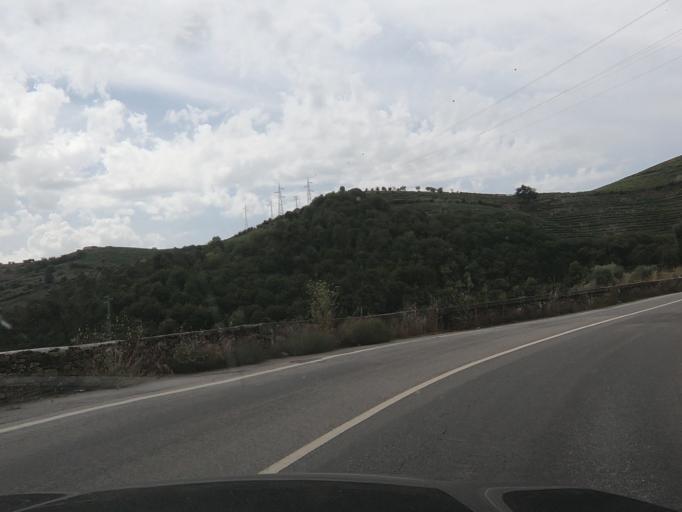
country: PT
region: Vila Real
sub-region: Santa Marta de Penaguiao
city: Santa Marta de Penaguiao
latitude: 41.2192
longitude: -7.7739
